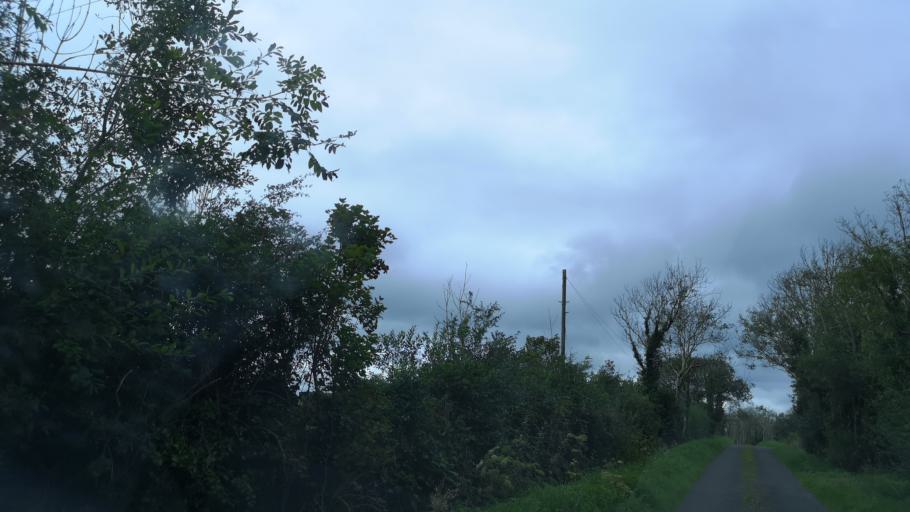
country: IE
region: Connaught
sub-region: County Galway
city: Athenry
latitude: 53.2973
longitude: -8.6673
